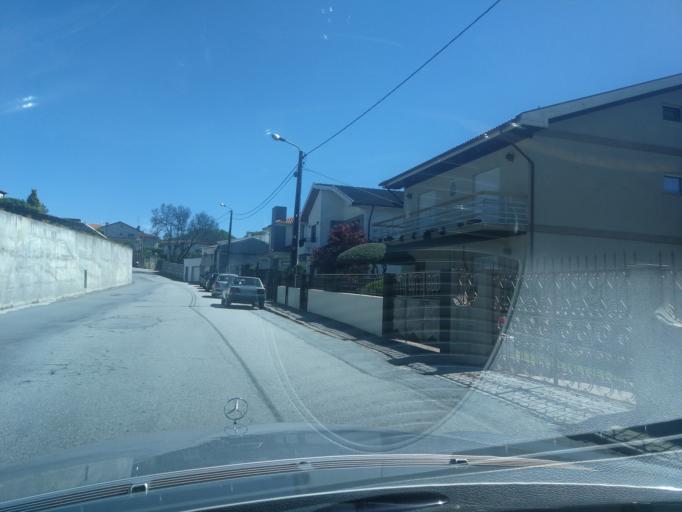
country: PT
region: Braga
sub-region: Braga
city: Adaufe
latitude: 41.5685
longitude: -8.4081
